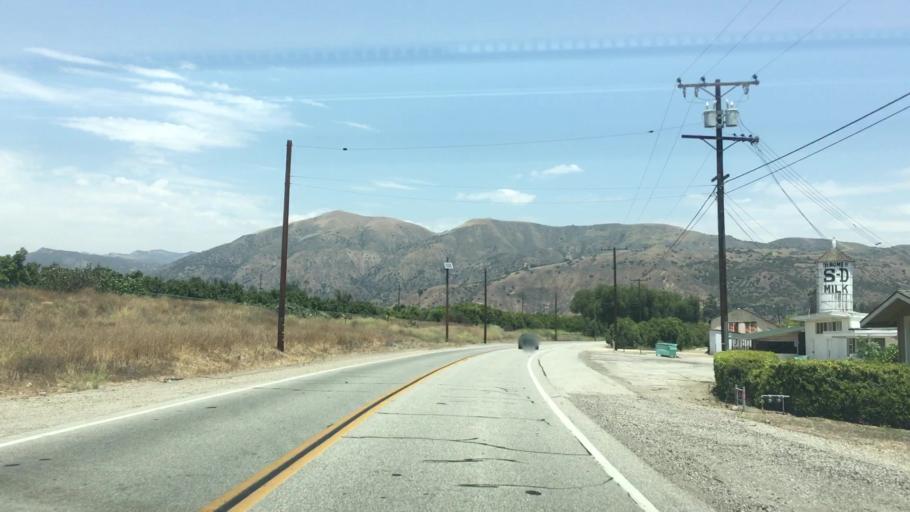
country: US
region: California
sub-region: Ventura County
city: Fillmore
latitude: 34.4071
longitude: -118.9427
